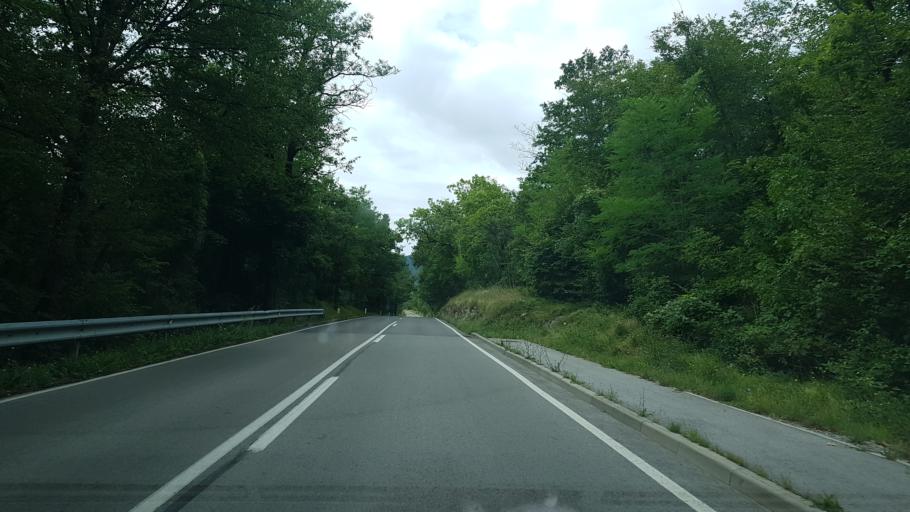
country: SI
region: Divaca
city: Divaca
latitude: 45.6785
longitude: 13.9548
